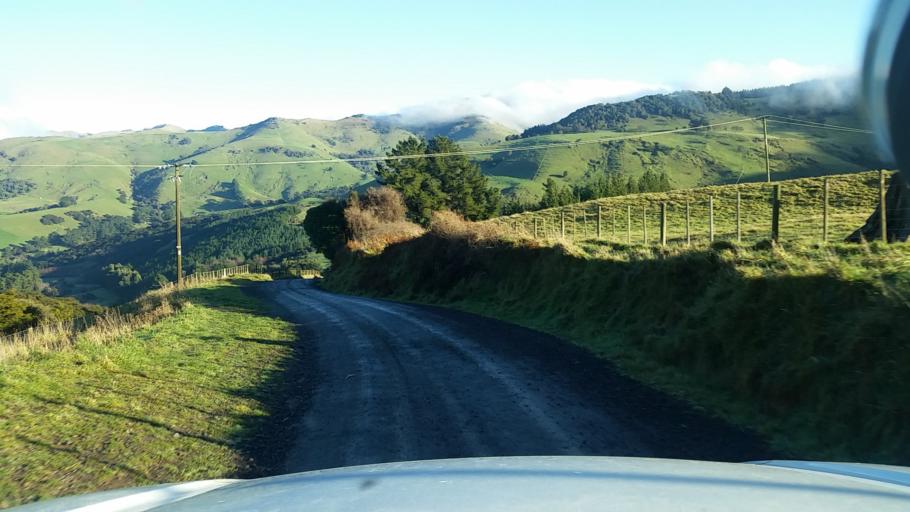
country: NZ
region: Canterbury
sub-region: Christchurch City
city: Christchurch
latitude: -43.7440
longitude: 172.8534
